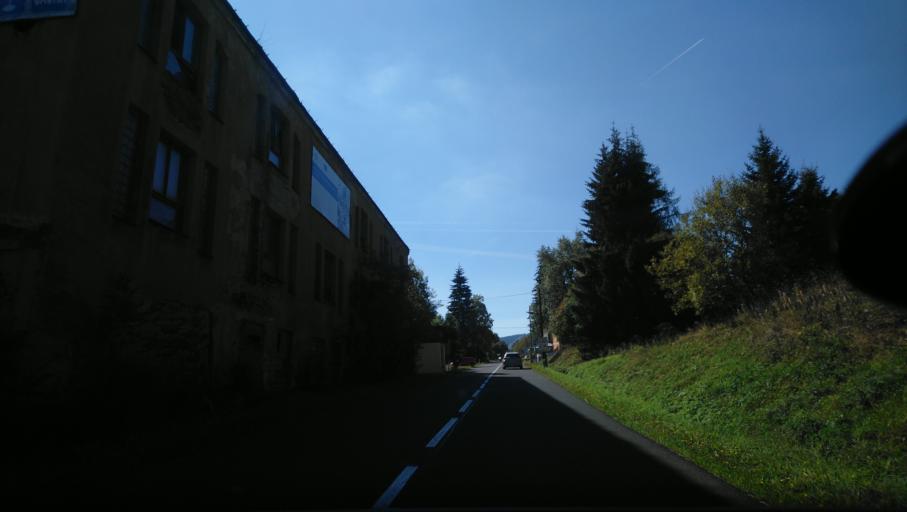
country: DE
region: Saxony
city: Kurort Oberwiesenthal
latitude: 50.4279
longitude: 13.0026
